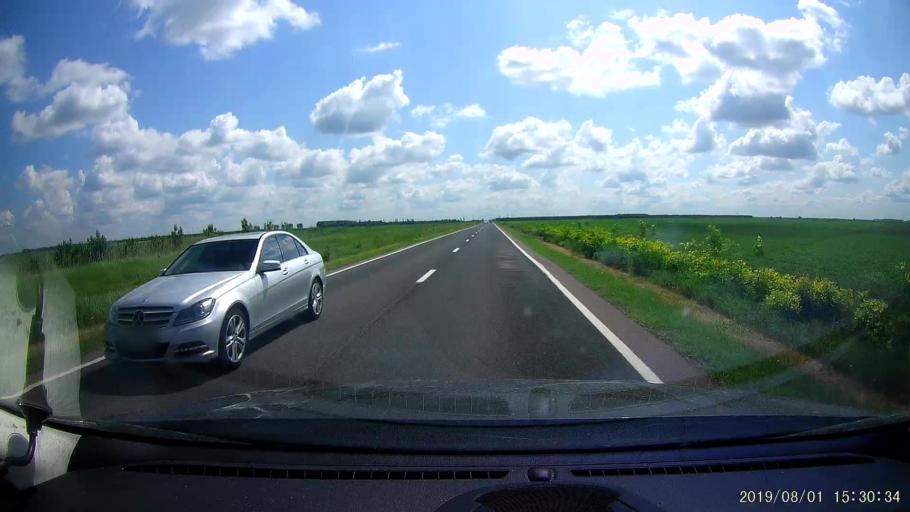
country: RO
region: Braila
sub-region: Comuna Viziru
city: Viziru
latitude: 44.9613
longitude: 27.6751
